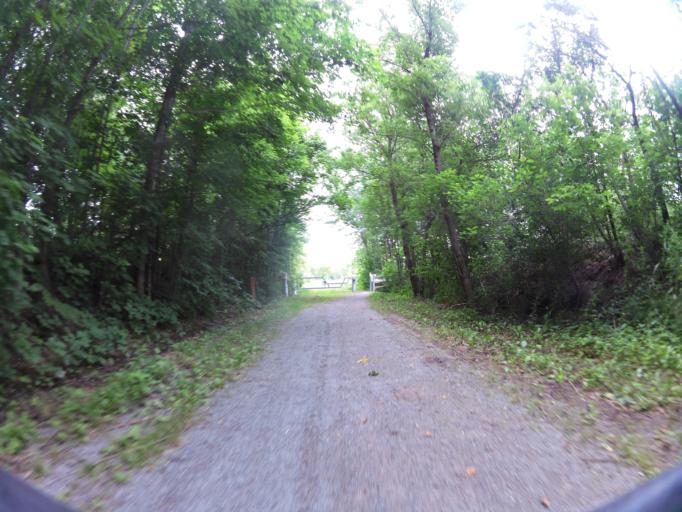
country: CA
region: Ontario
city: Ottawa
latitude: 45.2517
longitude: -75.6214
